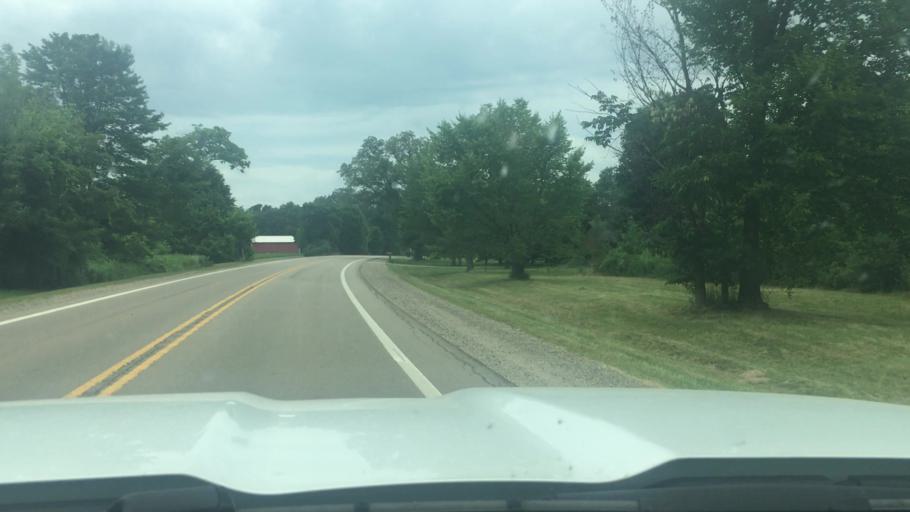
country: US
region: Michigan
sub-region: Clinton County
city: Fowler
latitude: 42.9956
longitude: -84.8635
